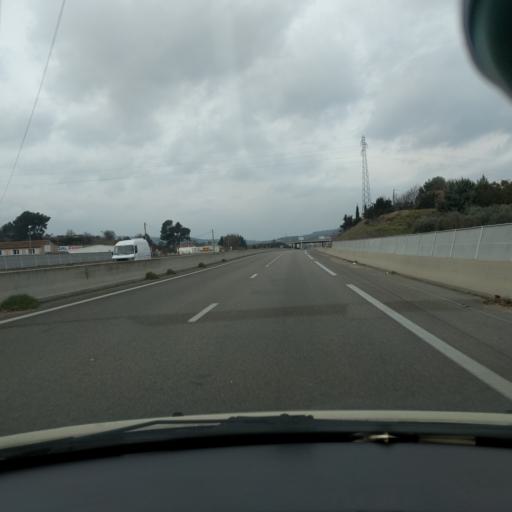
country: FR
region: Provence-Alpes-Cote d'Azur
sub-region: Departement des Bouches-du-Rhone
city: Meyreuil
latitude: 43.4731
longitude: 5.4867
